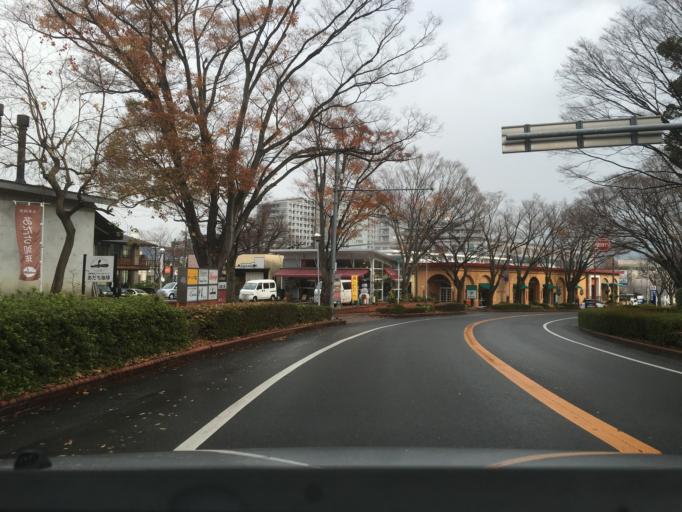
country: JP
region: Fukuoka
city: Kurume
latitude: 33.3253
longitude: 130.5073
